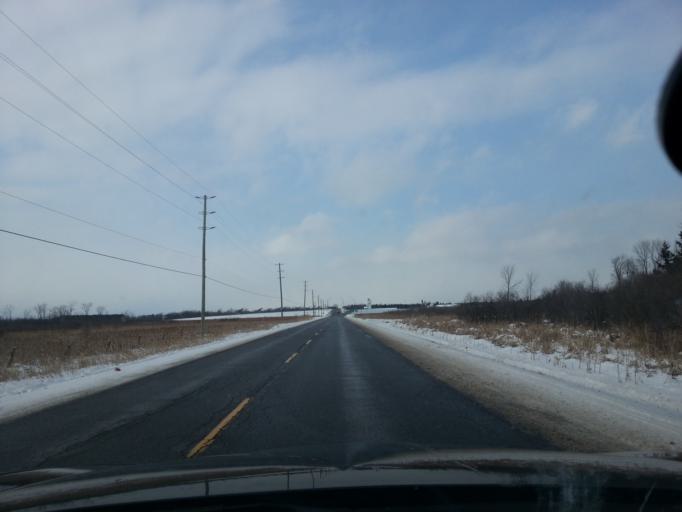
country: CA
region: Ontario
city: Carleton Place
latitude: 45.1657
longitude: -76.0434
